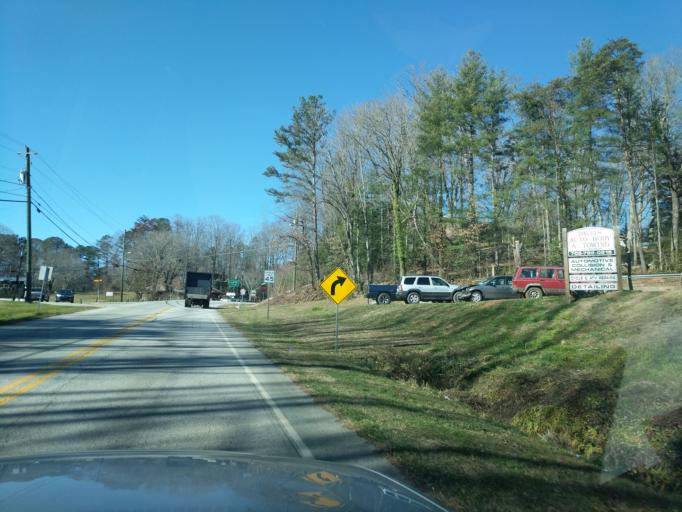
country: US
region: Georgia
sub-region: Rabun County
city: Clayton
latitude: 34.8637
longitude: -83.3940
